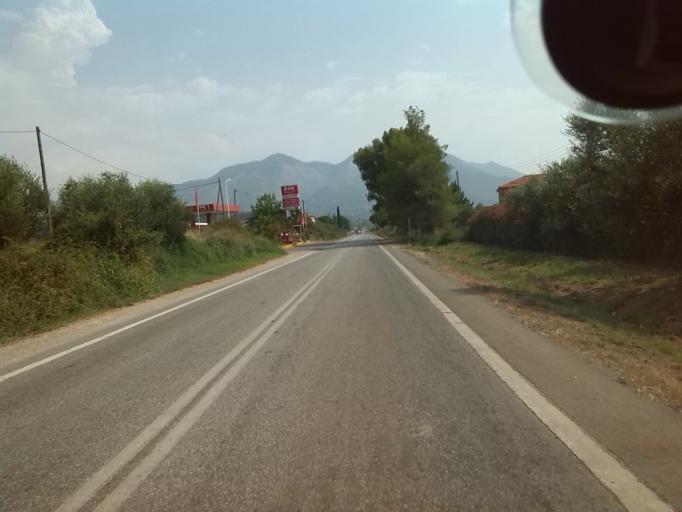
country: GR
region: Peloponnese
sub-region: Nomos Messinias
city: Kyparissia
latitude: 37.3026
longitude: 21.7023
